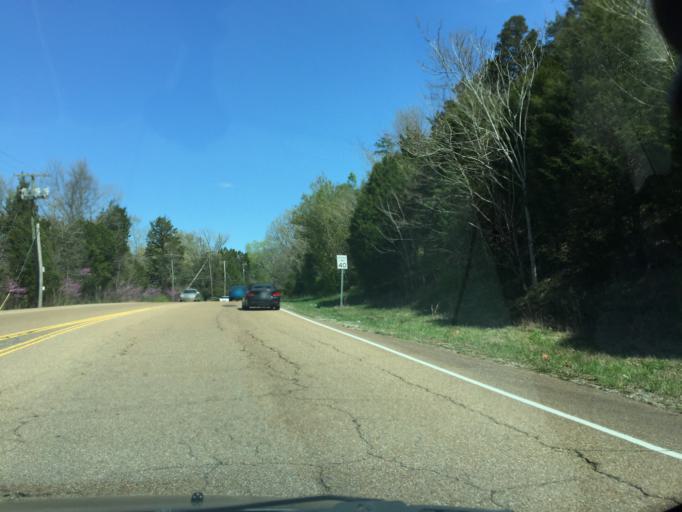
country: US
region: Tennessee
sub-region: Hamilton County
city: Middle Valley
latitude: 35.1539
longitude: -85.2186
